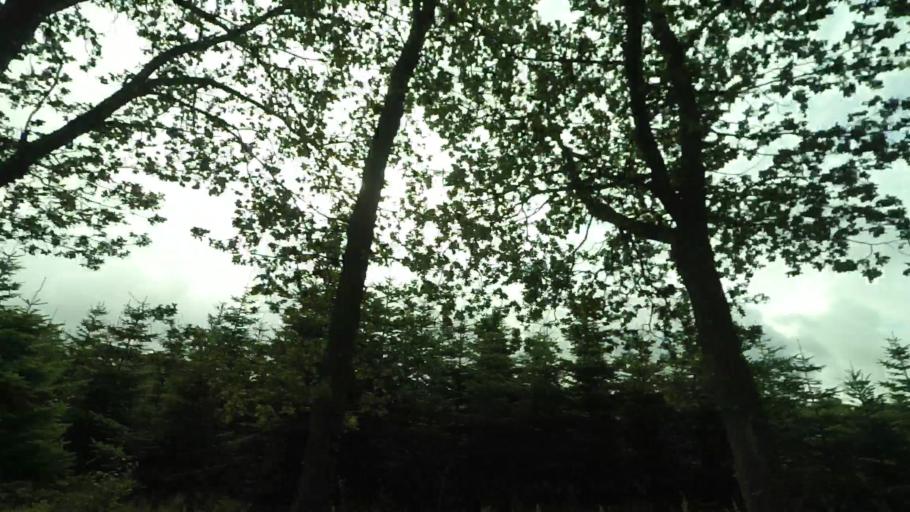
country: DK
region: Central Jutland
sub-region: Syddjurs Kommune
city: Ronde
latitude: 56.3401
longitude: 10.4850
